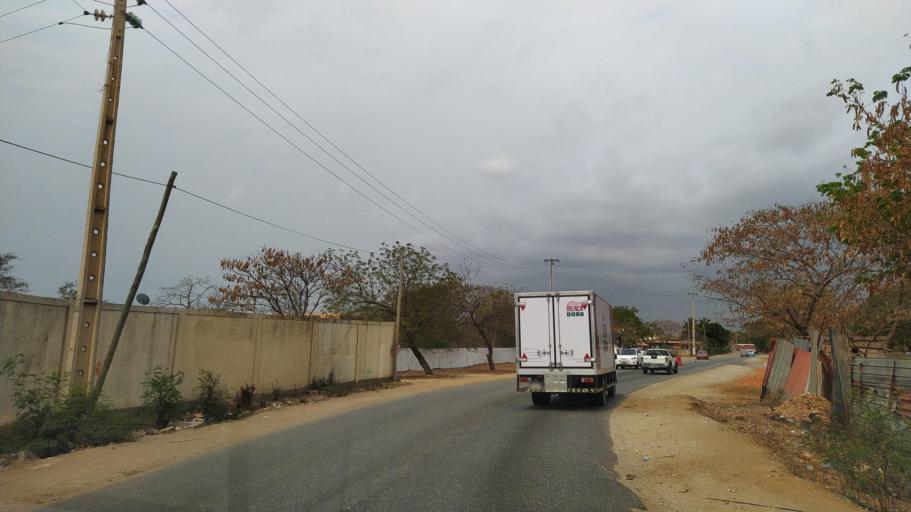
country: AO
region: Luanda
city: Luanda
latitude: -8.8576
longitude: 13.2856
